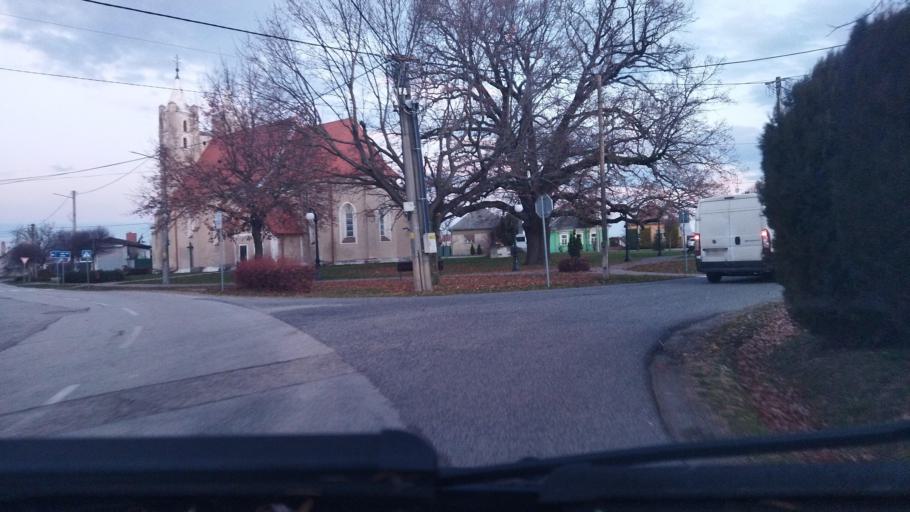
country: SK
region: Trnavsky
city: Dunajska Streda
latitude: 47.9951
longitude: 17.4846
